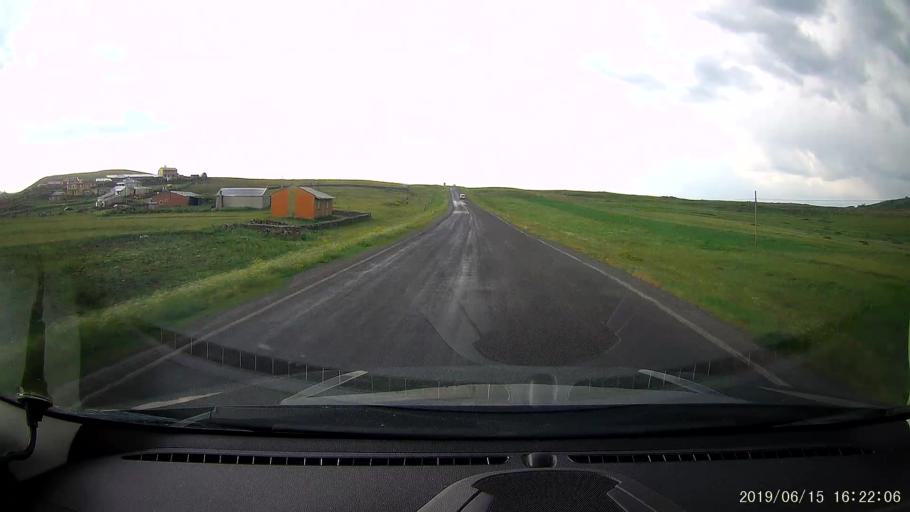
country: TR
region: Ardahan
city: Hanak
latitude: 41.1915
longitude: 42.8465
